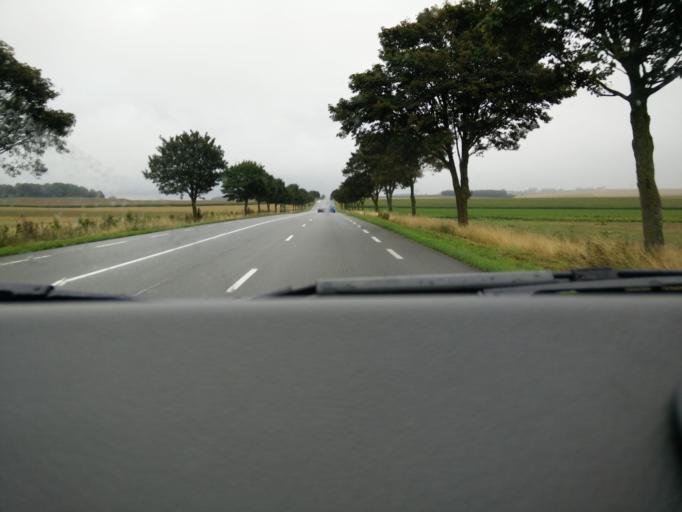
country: FR
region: Nord-Pas-de-Calais
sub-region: Departement du Pas-de-Calais
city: Saint-Pol-sur-Ternoise
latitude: 50.3893
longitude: 2.2356
